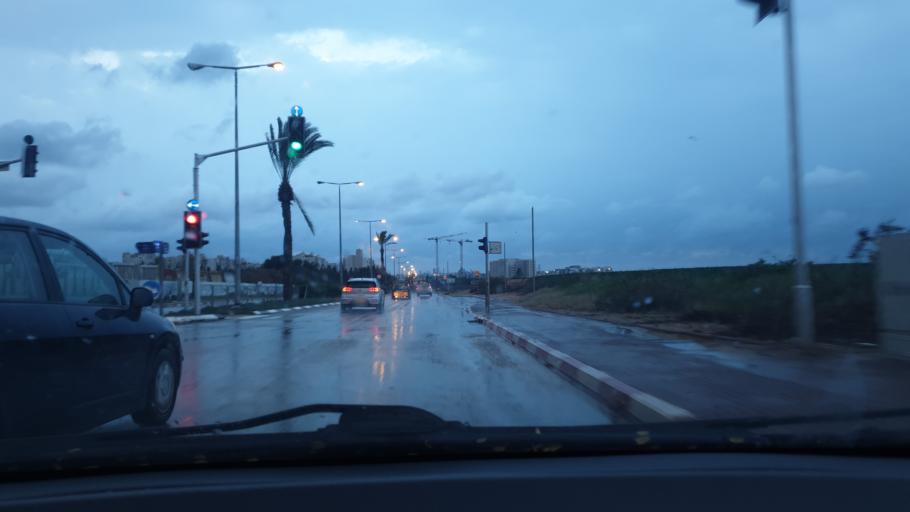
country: IL
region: Central District
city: Bet Dagan
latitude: 31.9717
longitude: 34.8230
